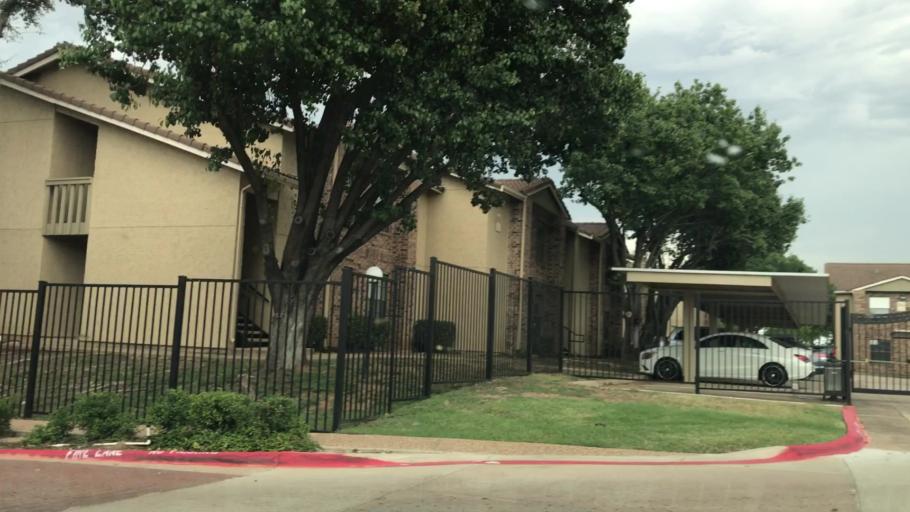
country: US
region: Texas
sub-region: Dallas County
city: Farmers Branch
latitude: 32.9066
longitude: -96.9600
